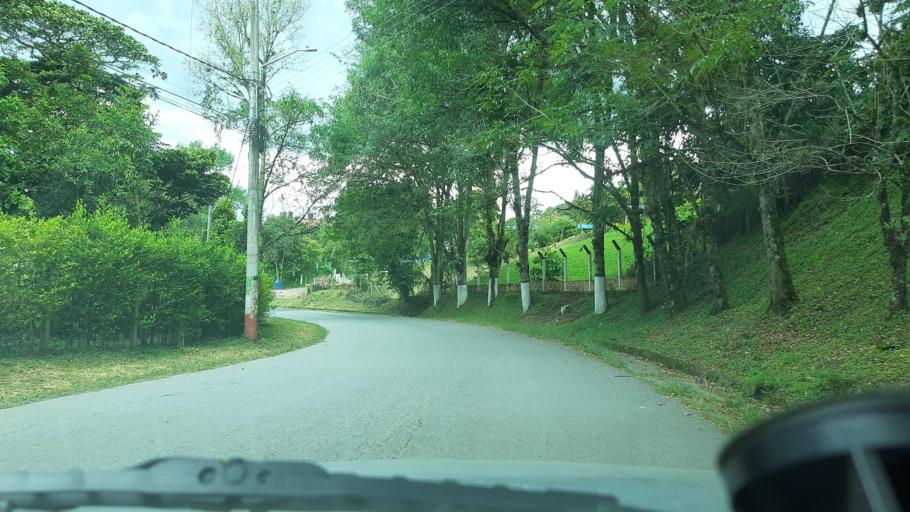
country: CO
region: Boyaca
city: Moniquira
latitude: 5.8862
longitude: -73.5776
